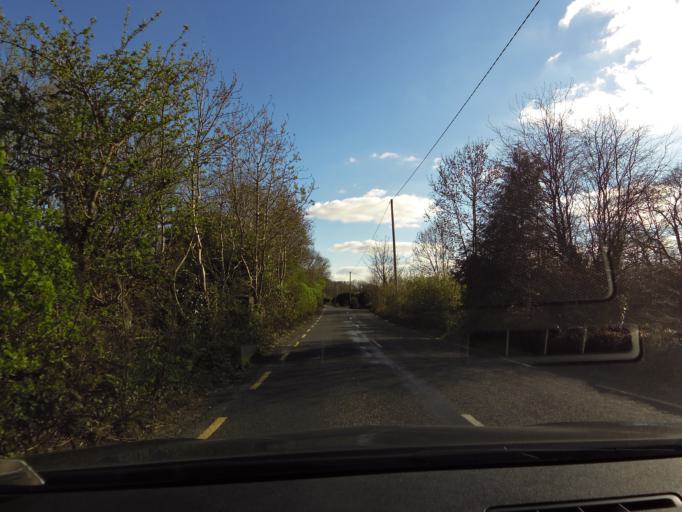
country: IE
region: Connaught
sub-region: County Galway
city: Portumna
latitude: 53.0938
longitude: -8.1837
